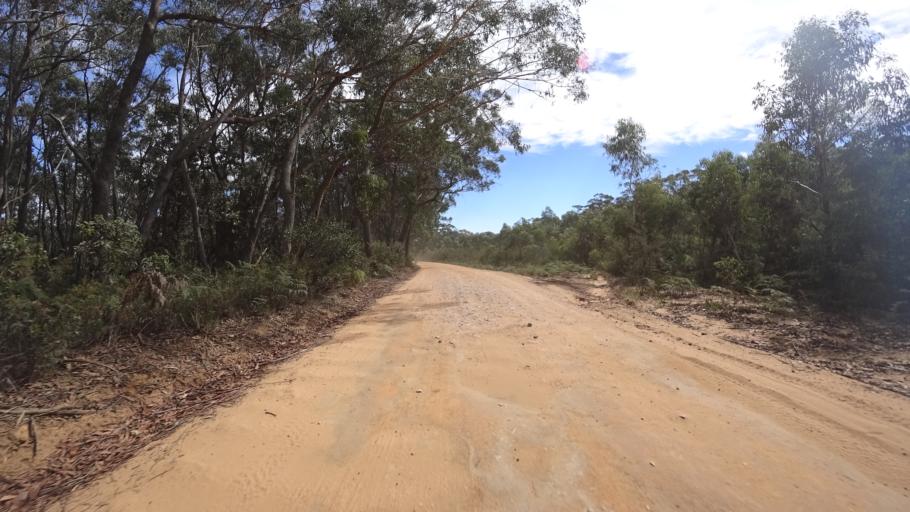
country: AU
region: New South Wales
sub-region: Lithgow
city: Lithgow
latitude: -33.3309
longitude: 150.2496
